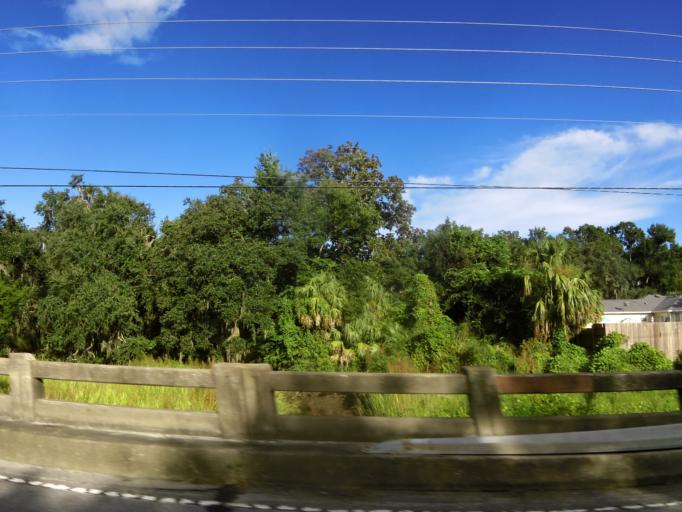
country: US
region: Georgia
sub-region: Glynn County
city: Country Club Estates
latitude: 31.2452
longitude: -81.4497
